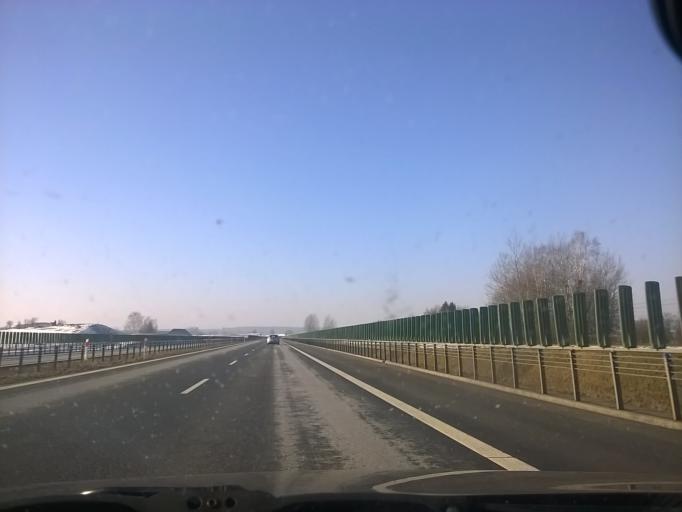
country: PL
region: Warmian-Masurian Voivodeship
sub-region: Powiat olsztynski
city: Biskupiec
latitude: 53.8349
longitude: 21.0340
